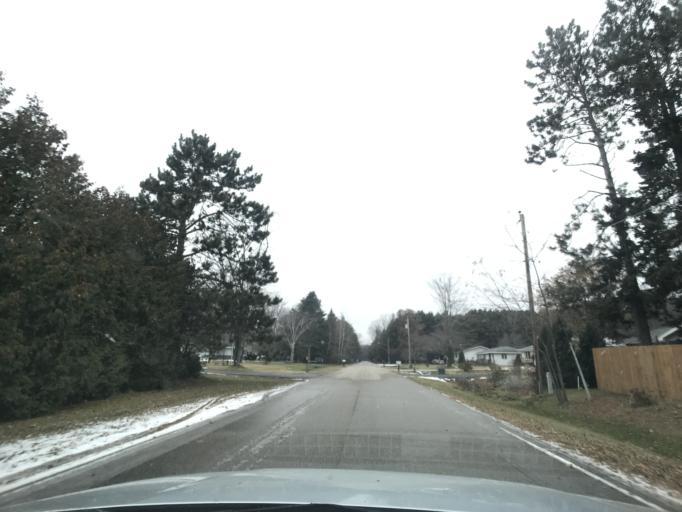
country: US
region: Wisconsin
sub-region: Marinette County
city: Marinette
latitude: 45.0483
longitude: -87.6259
